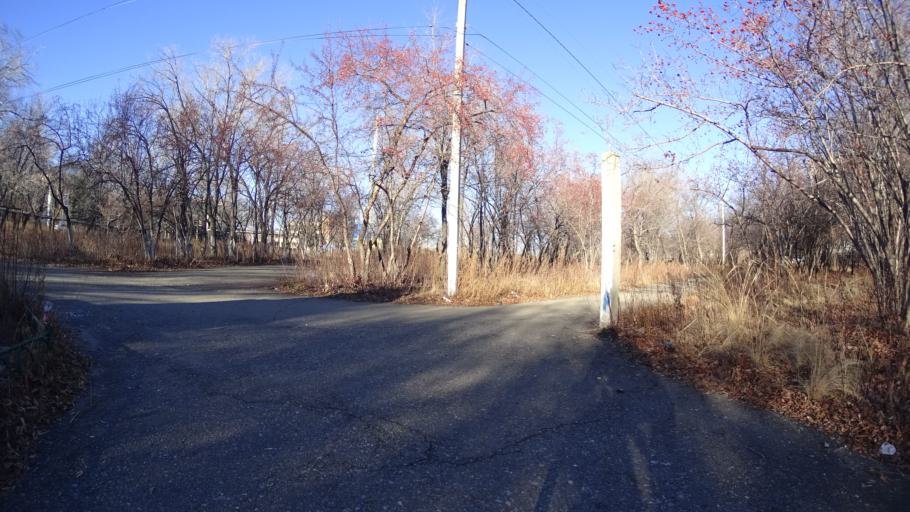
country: RU
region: Chelyabinsk
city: Troitsk
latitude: 54.1017
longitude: 61.5560
